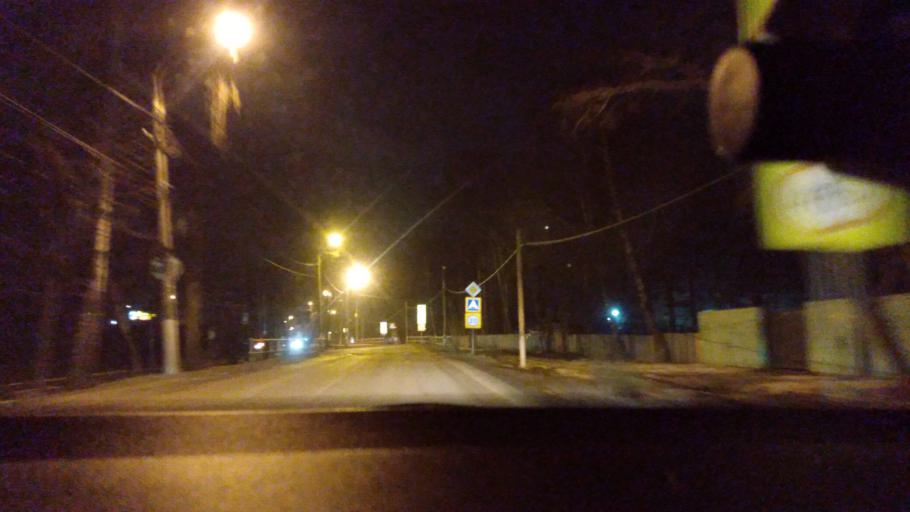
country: RU
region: Moskovskaya
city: Saltykovka
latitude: 55.7657
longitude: 37.9233
